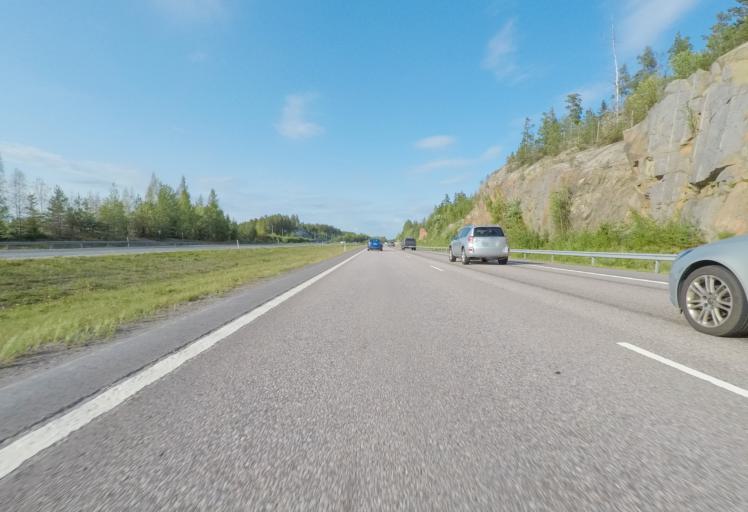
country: FI
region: Uusimaa
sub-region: Porvoo
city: Pukkila
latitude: 60.7303
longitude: 25.4448
